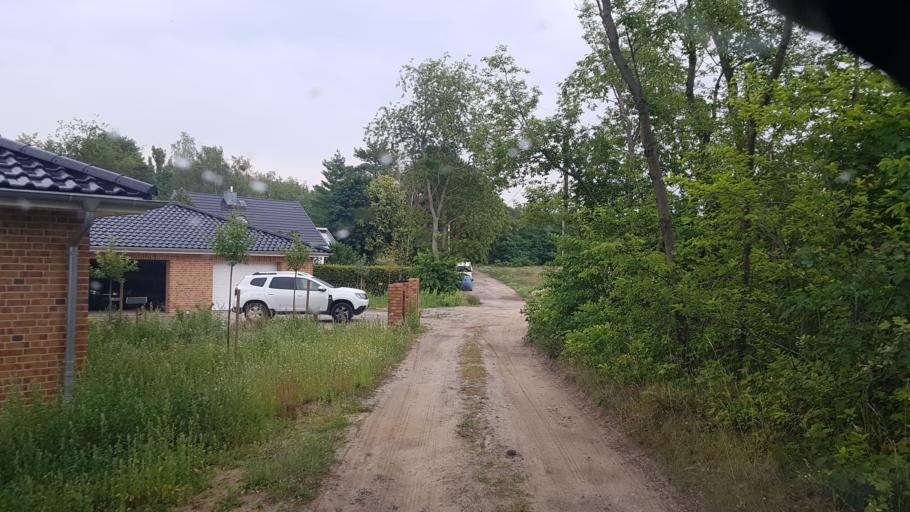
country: DE
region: Brandenburg
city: Teupitz
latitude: 52.1371
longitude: 13.6278
